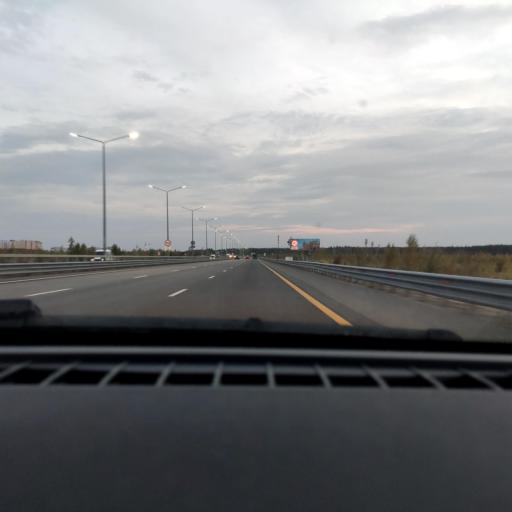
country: RU
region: Voronezj
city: Somovo
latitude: 51.7556
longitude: 39.3065
